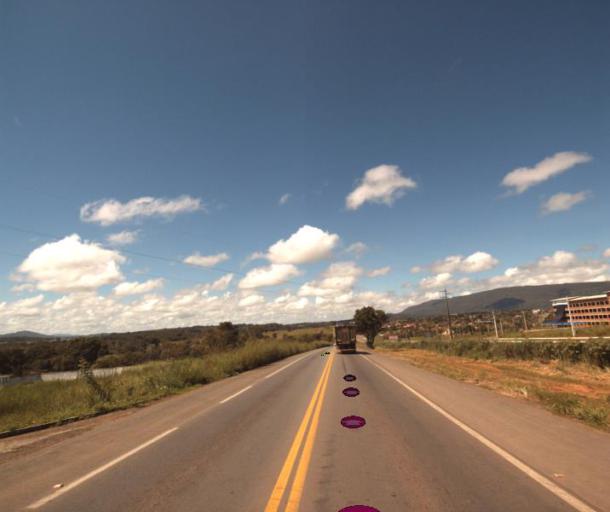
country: BR
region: Goias
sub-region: Jaragua
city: Jaragua
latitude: -15.7415
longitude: -49.3206
